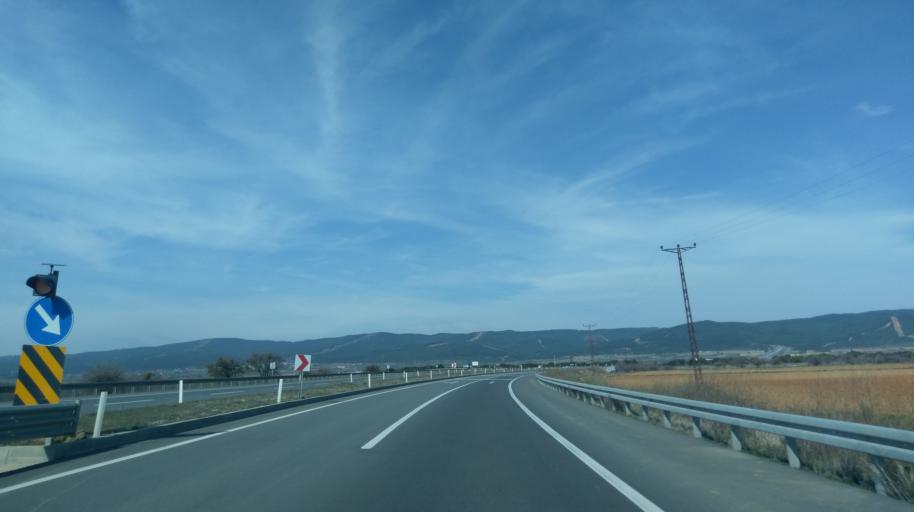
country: TR
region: Canakkale
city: Evrese
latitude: 40.6643
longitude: 26.8081
